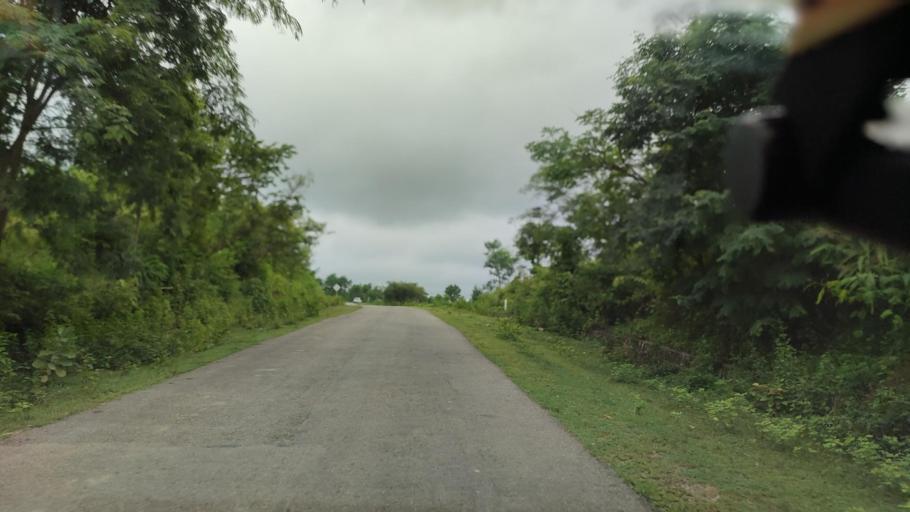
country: MM
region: Magway
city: Taungdwingyi
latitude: 19.9966
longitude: 95.8865
